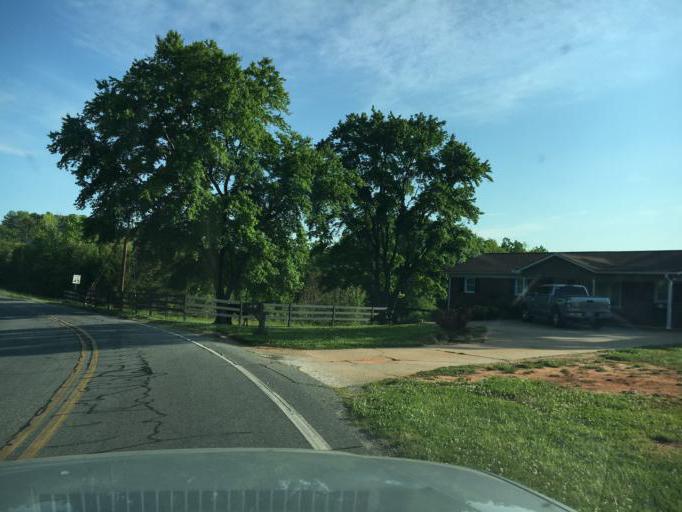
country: US
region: North Carolina
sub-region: Rutherford County
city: Rutherfordton
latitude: 35.3393
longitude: -81.9854
